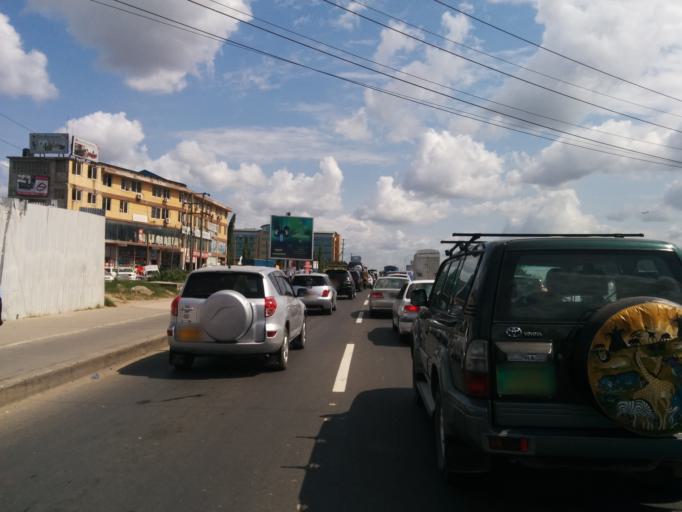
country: TZ
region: Dar es Salaam
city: Dar es Salaam
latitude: -6.8295
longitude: 39.2731
